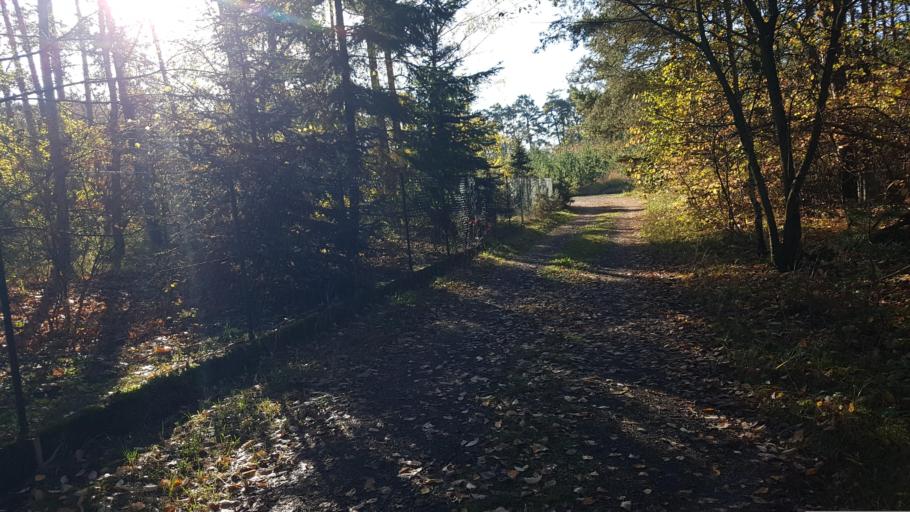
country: DE
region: Brandenburg
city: Schlieben
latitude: 51.7404
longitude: 13.3868
